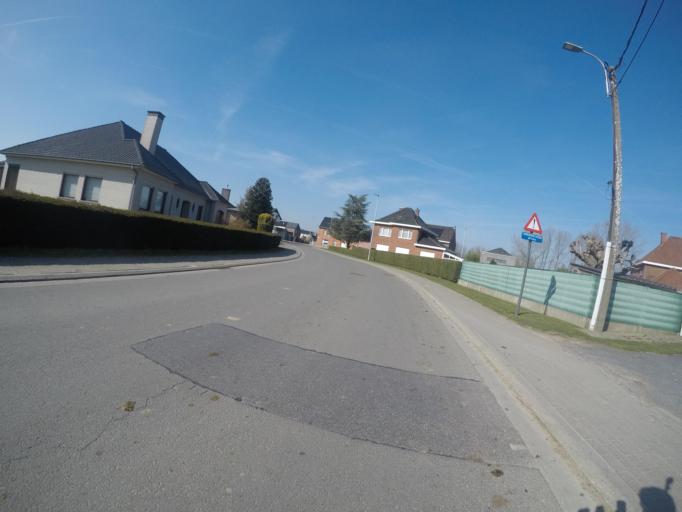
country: BE
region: Flanders
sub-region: Provincie Oost-Vlaanderen
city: Sint-Maria-Lierde
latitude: 50.8011
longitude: 3.8285
